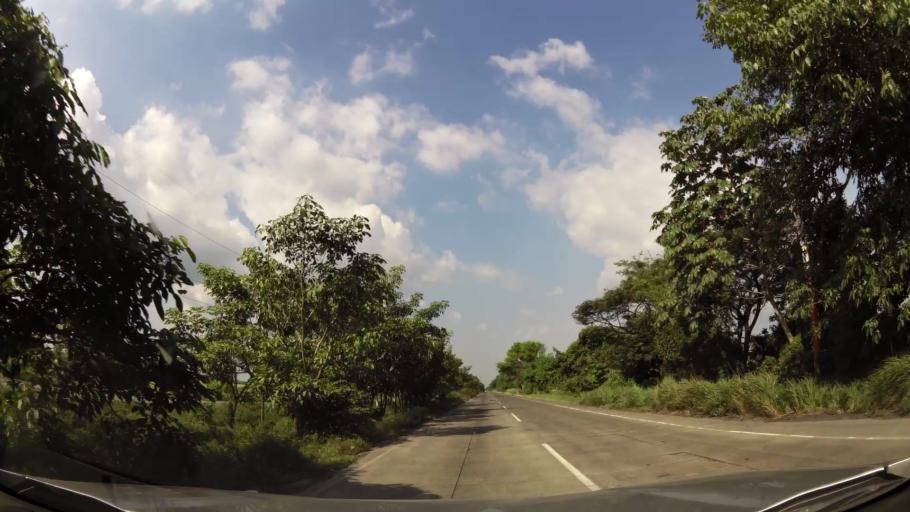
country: GT
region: Escuintla
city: Puerto San Jose
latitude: 14.0227
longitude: -90.7826
